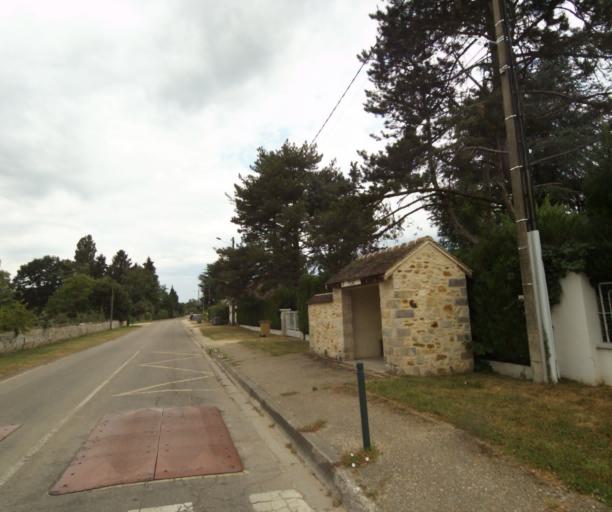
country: FR
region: Ile-de-France
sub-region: Departement de Seine-et-Marne
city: Arbonne-la-Foret
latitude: 48.4429
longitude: 2.5580
